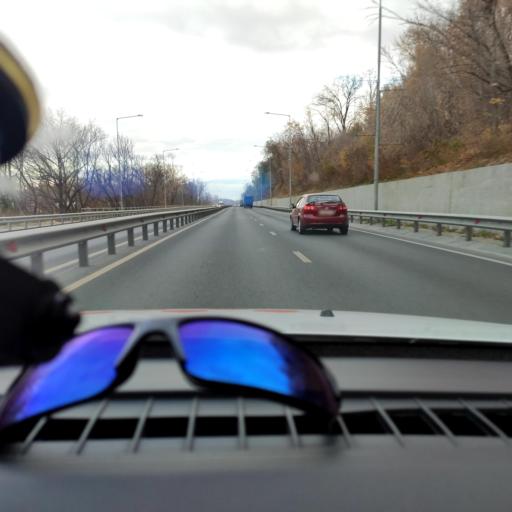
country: RU
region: Samara
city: Volzhskiy
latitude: 53.3902
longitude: 50.1587
